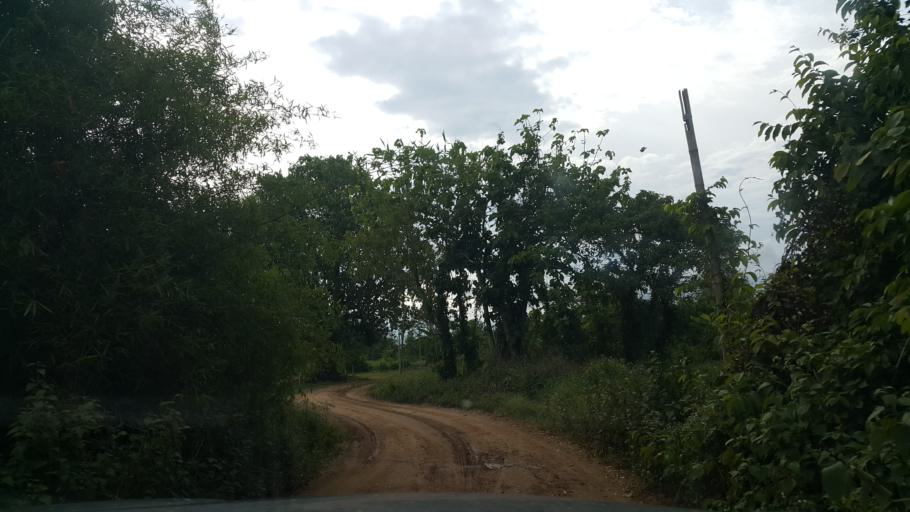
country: TH
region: Chiang Rai
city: Wiang Chai
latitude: 19.9739
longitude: 99.9145
